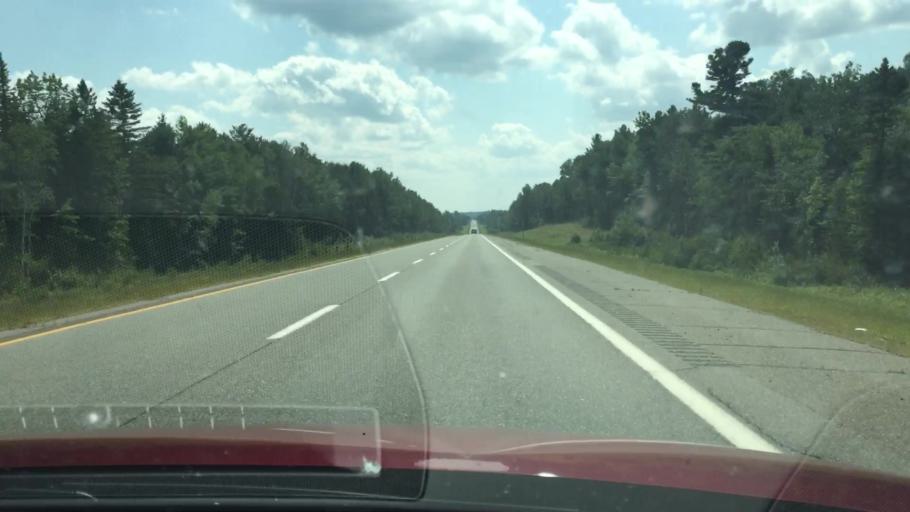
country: US
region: Maine
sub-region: Penobscot County
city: Lincoln
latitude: 45.4130
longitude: -68.5944
